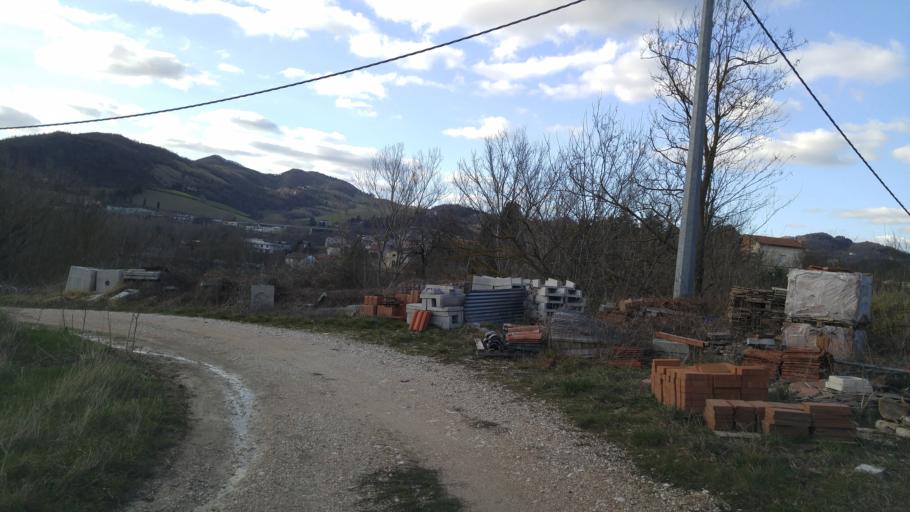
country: IT
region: The Marches
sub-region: Provincia di Pesaro e Urbino
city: Cagli
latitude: 43.5498
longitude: 12.6553
